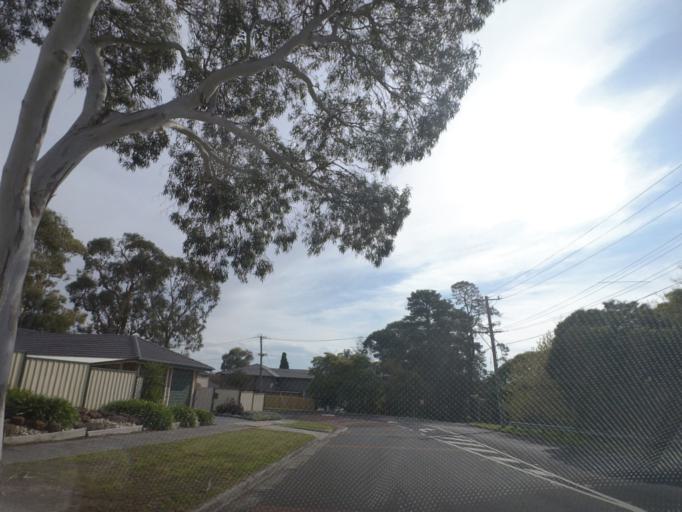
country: AU
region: Victoria
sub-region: Whitehorse
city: Vermont
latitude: -37.8475
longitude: 145.1974
